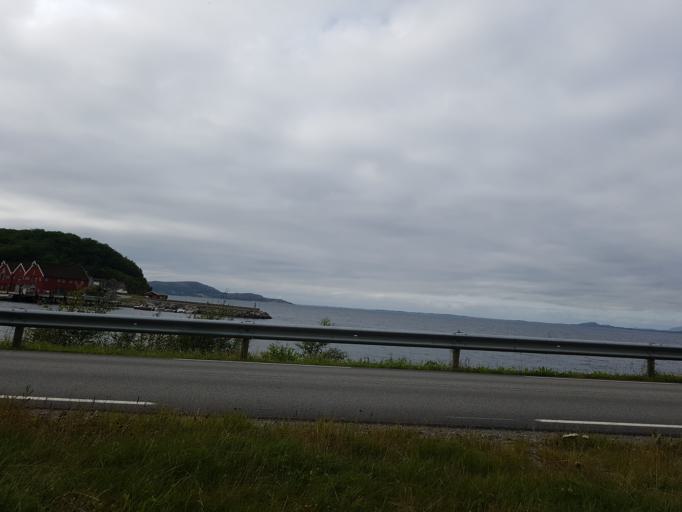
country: NO
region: Sor-Trondelag
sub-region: Agdenes
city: Lensvik
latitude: 63.6337
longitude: 9.8310
